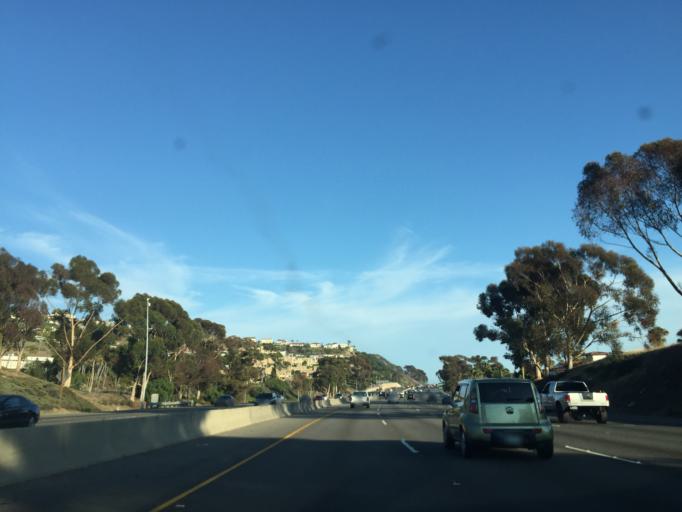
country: US
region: California
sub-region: Orange County
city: San Clemente
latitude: 33.4291
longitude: -117.6122
